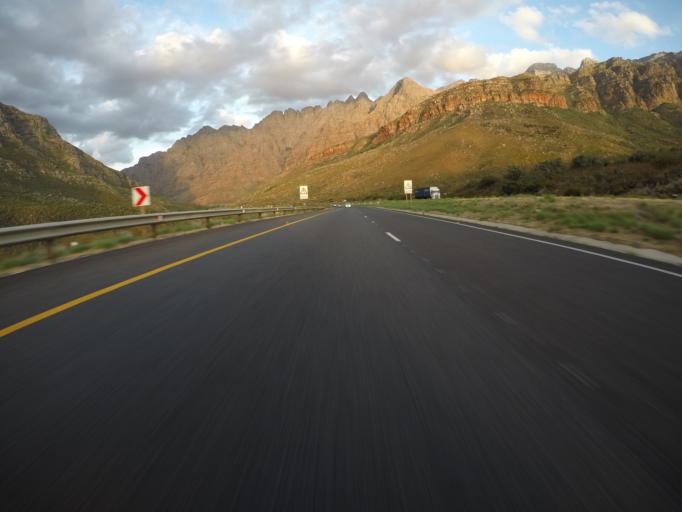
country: ZA
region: Western Cape
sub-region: Cape Winelands District Municipality
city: Paarl
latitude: -33.7246
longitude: 19.1639
